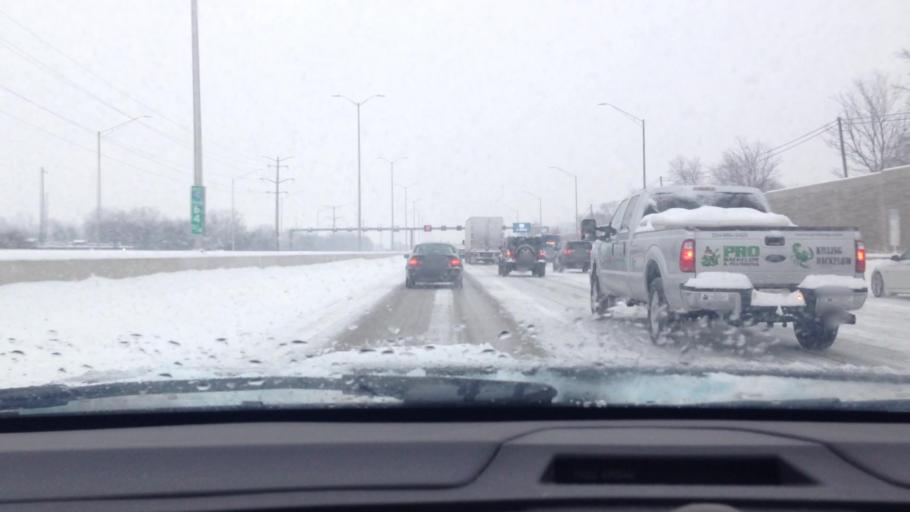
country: US
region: Illinois
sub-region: Cook County
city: Hoffman Estates
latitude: 42.0633
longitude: -88.0989
